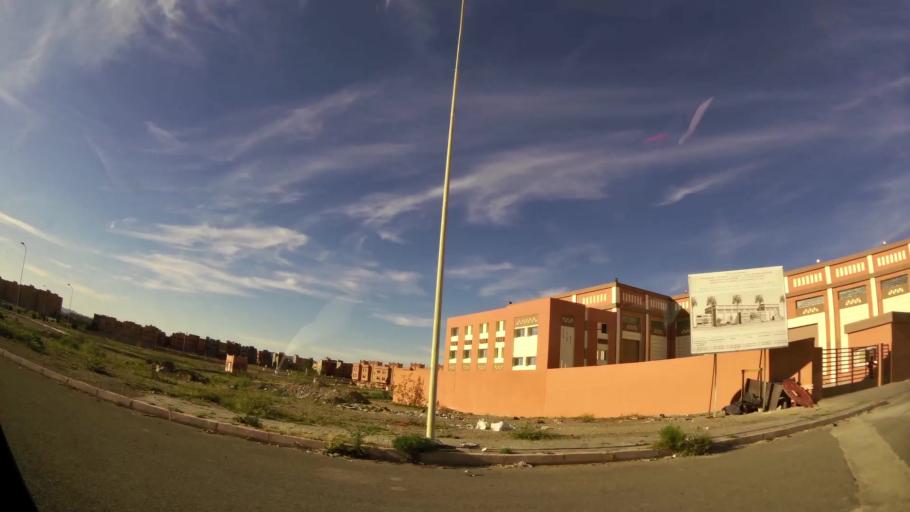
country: MA
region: Marrakech-Tensift-Al Haouz
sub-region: Marrakech
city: Marrakesh
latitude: 31.7542
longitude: -8.0991
